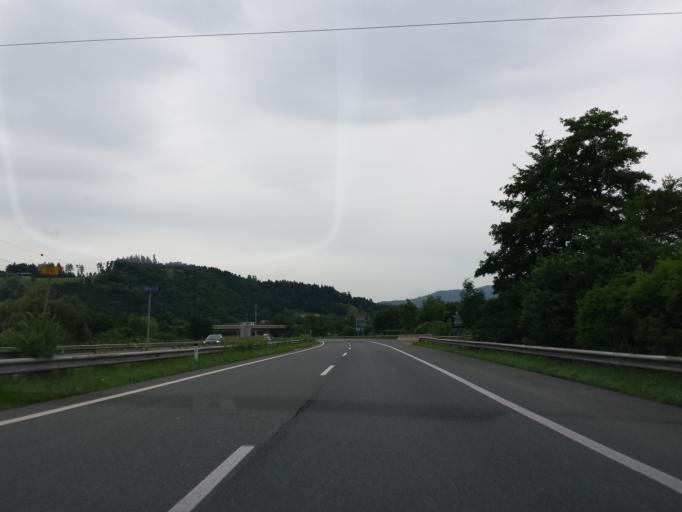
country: AT
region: Styria
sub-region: Politischer Bezirk Graz-Umgebung
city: Deutschfeistritz
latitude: 47.1851
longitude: 15.3315
